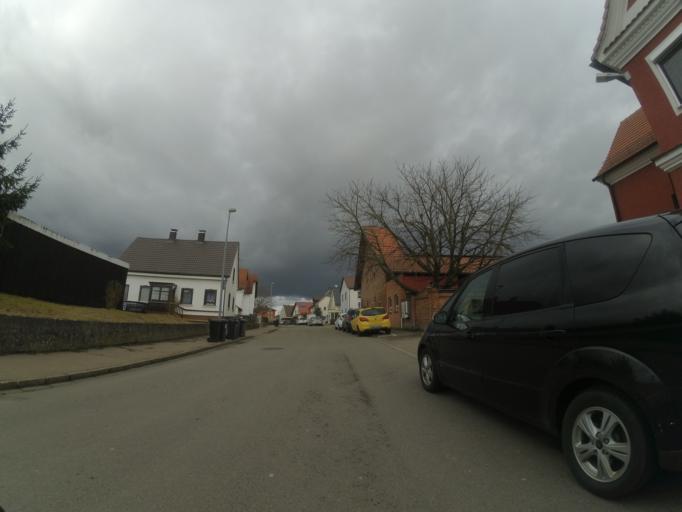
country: DE
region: Bavaria
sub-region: Swabia
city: Vohringen
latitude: 48.3156
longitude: 10.1042
